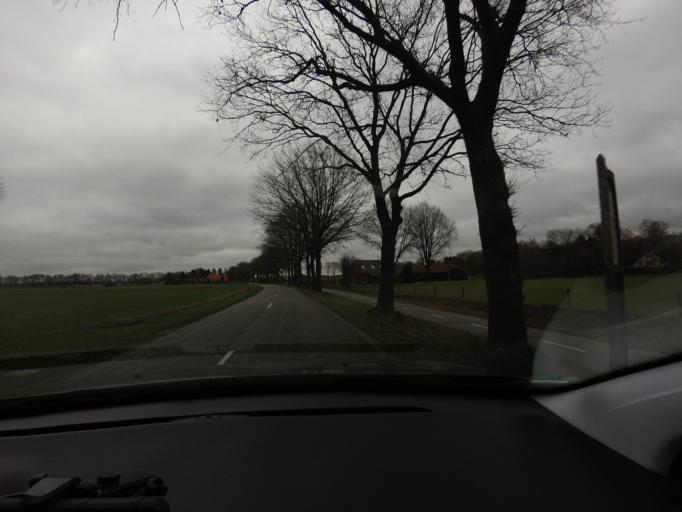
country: NL
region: Drenthe
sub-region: Gemeente Hoogeveen
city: Hoogeveen
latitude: 52.8305
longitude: 6.5235
